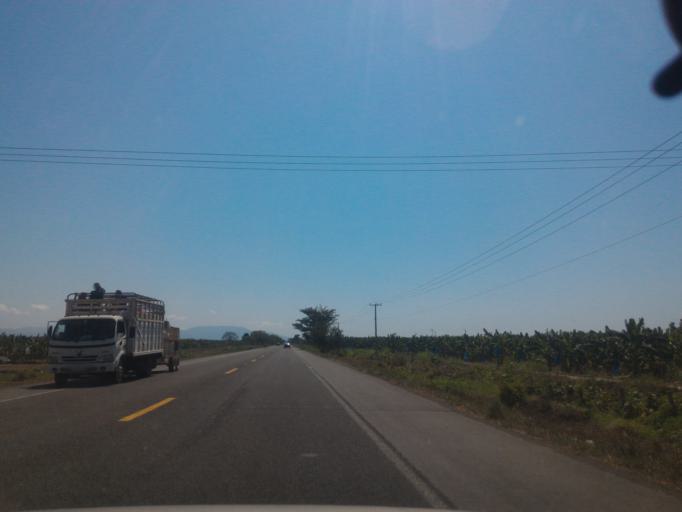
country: MX
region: Colima
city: Tecoman
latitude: 18.8147
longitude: -103.8058
